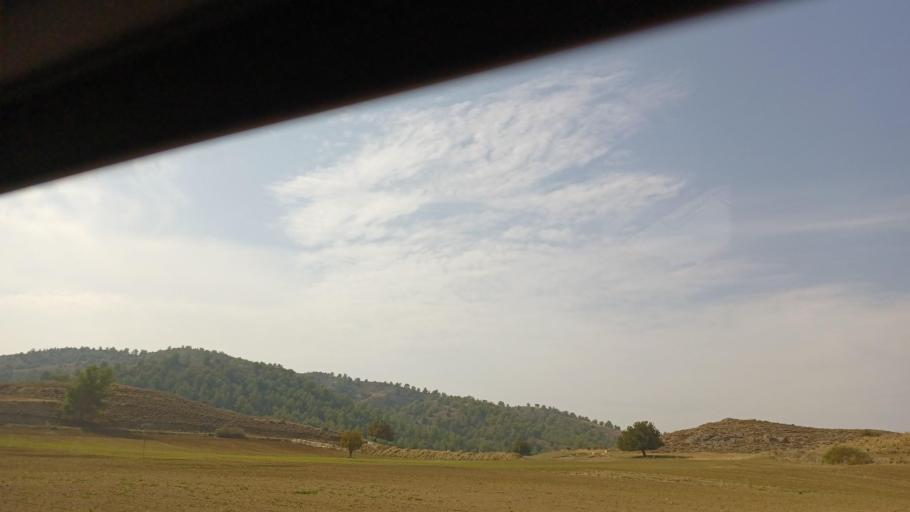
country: CY
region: Larnaka
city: Mosfiloti
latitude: 34.9676
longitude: 33.4399
